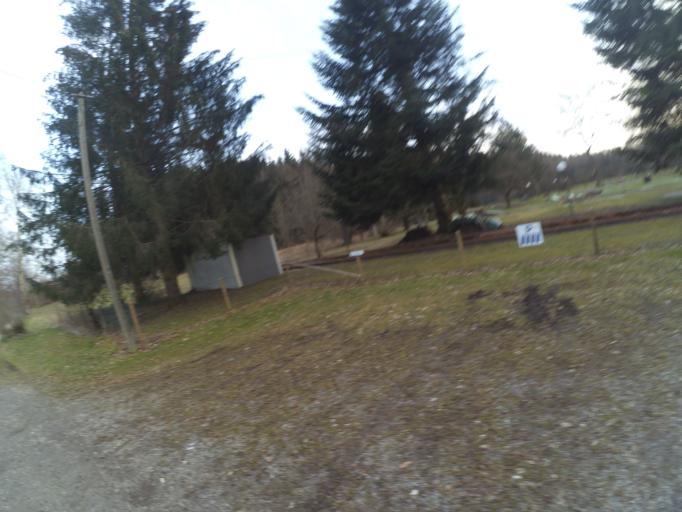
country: DE
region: Bavaria
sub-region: Swabia
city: Bad Worishofen
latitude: 47.9949
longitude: 10.5708
